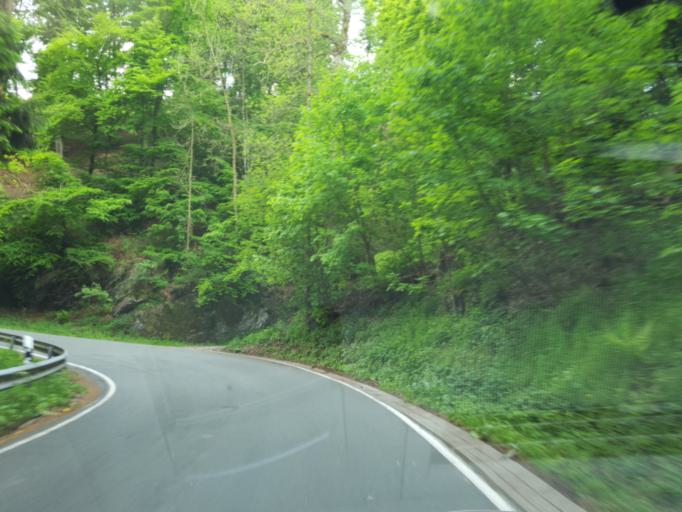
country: DE
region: North Rhine-Westphalia
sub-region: Regierungsbezirk Arnsberg
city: Olsberg
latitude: 51.2786
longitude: 8.4712
